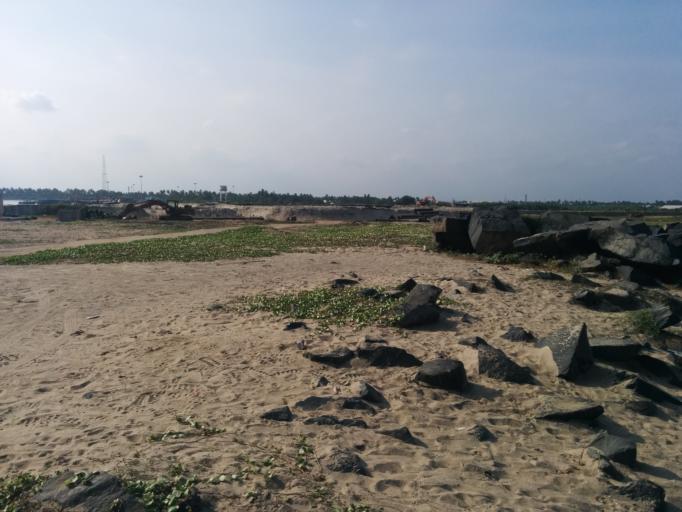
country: IN
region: Pondicherry
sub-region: Puducherry
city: Puducherry
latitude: 11.9073
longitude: 79.8296
